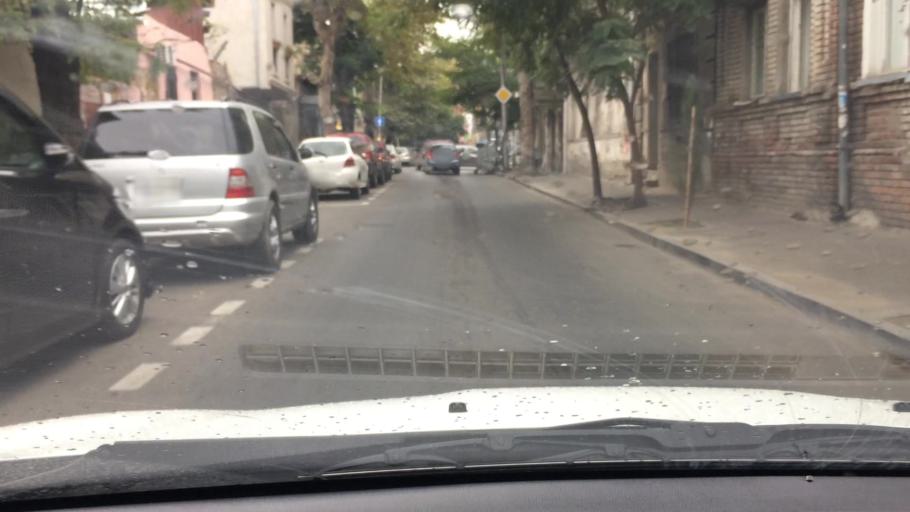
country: GE
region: T'bilisi
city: Tbilisi
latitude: 41.7105
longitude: 44.8025
